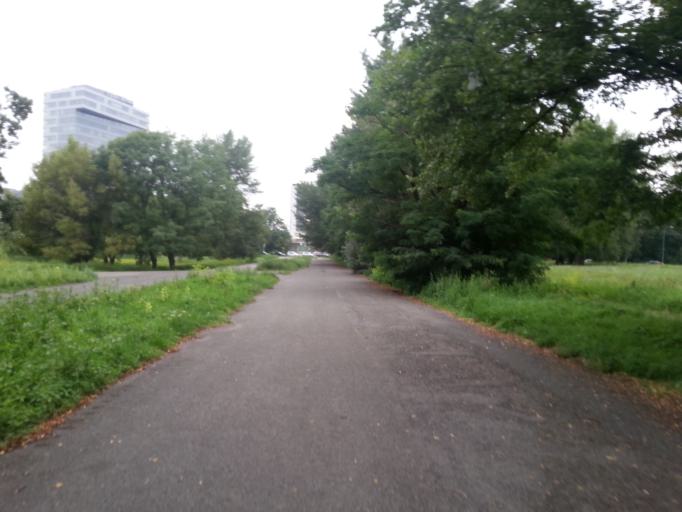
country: SK
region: Bratislavsky
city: Bratislava
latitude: 48.1284
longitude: 17.1189
